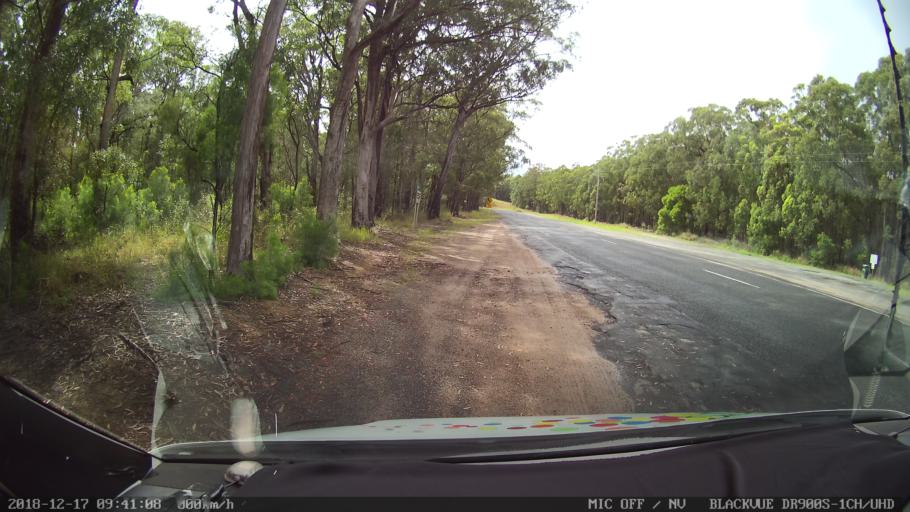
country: AU
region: New South Wales
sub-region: Tenterfield Municipality
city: Carrolls Creek
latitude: -28.9243
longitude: 152.3147
